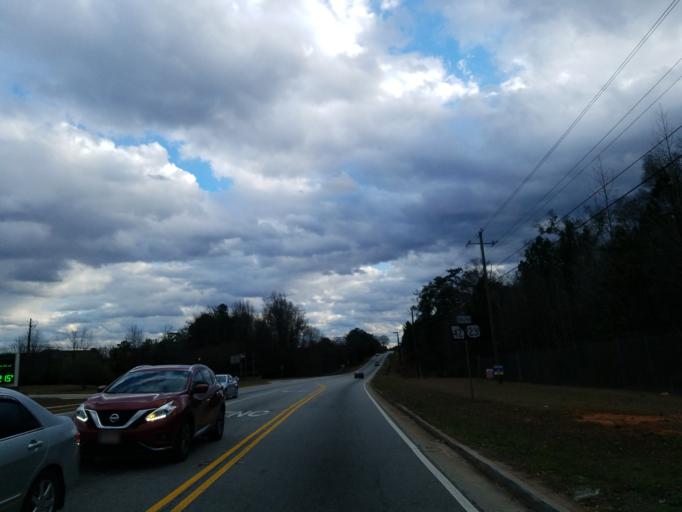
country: US
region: Georgia
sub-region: Henry County
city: McDonough
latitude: 33.4263
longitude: -84.1441
